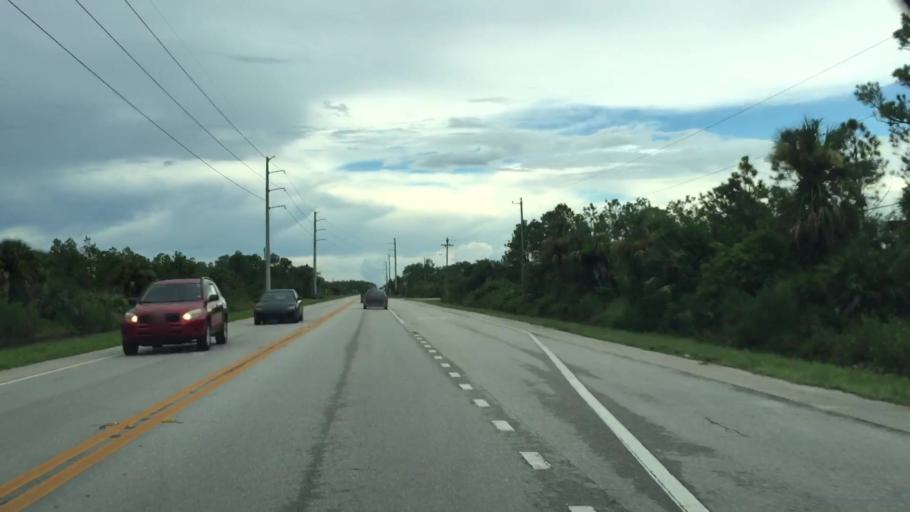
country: US
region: Florida
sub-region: Collier County
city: Orangetree
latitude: 26.3159
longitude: -81.5949
